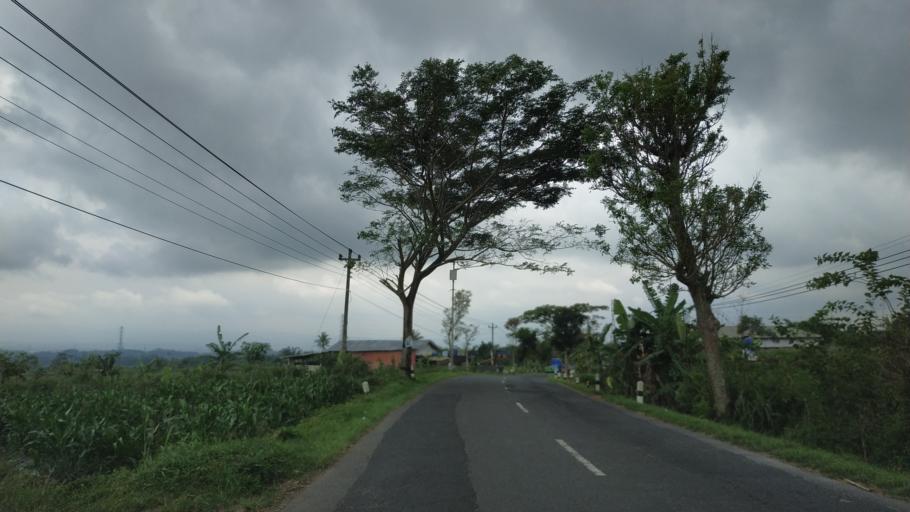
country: ID
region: Central Java
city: Magelang
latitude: -7.2862
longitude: 110.1216
